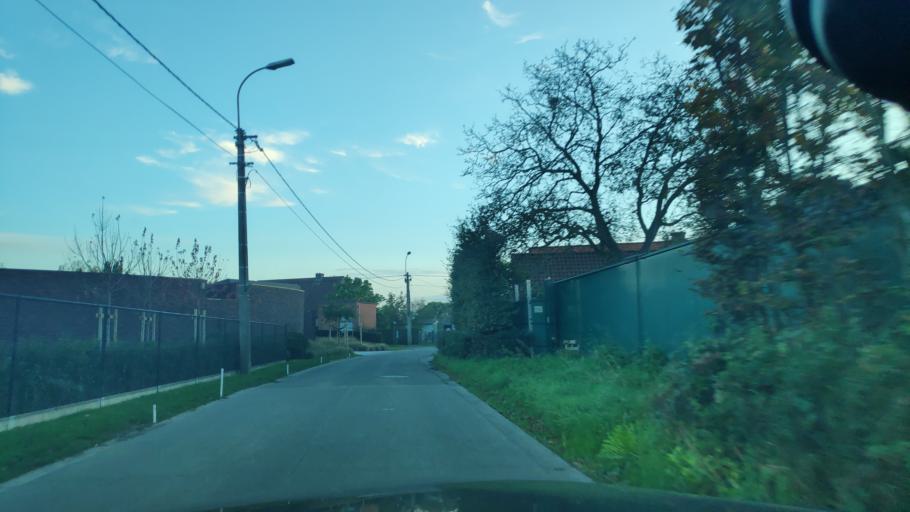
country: BE
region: Flanders
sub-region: Provincie Oost-Vlaanderen
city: Aalter
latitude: 51.1057
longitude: 3.5007
